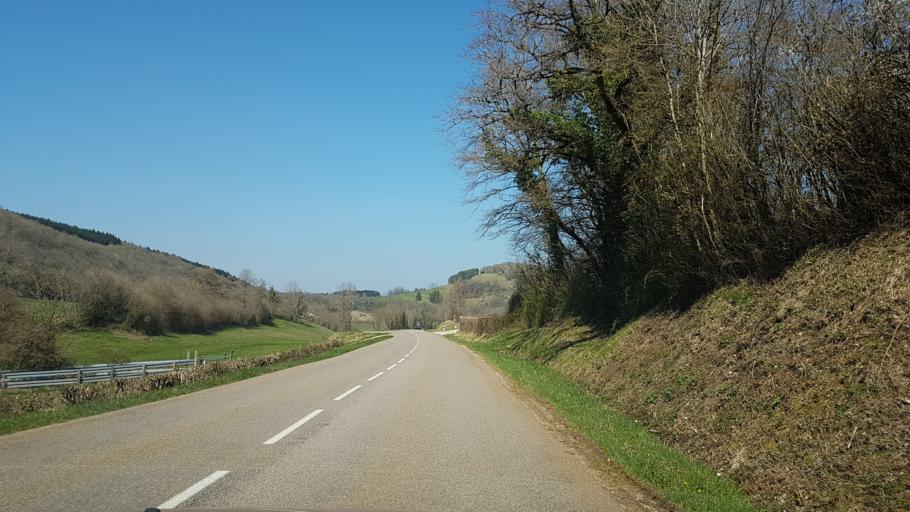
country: FR
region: Franche-Comte
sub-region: Departement du Jura
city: Orgelet
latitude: 46.5527
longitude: 5.6558
